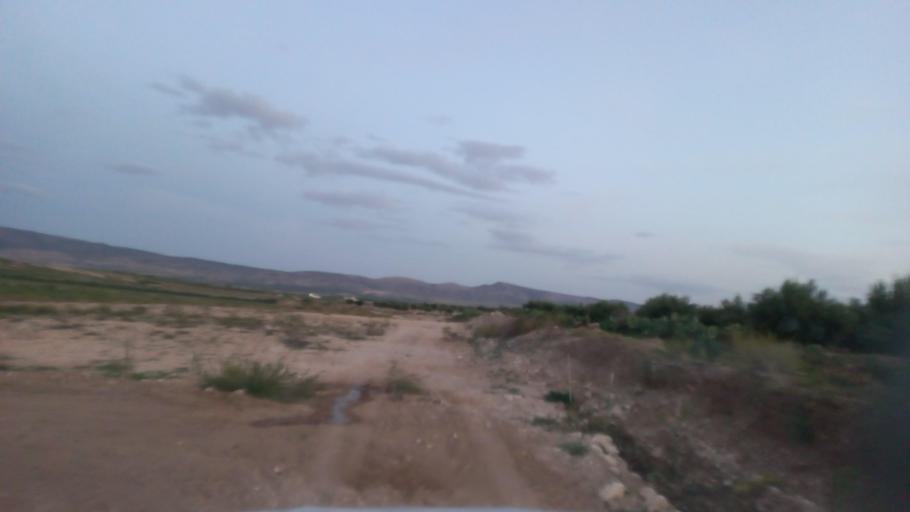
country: TN
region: Al Qasrayn
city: Sbiba
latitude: 35.4232
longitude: 9.1093
